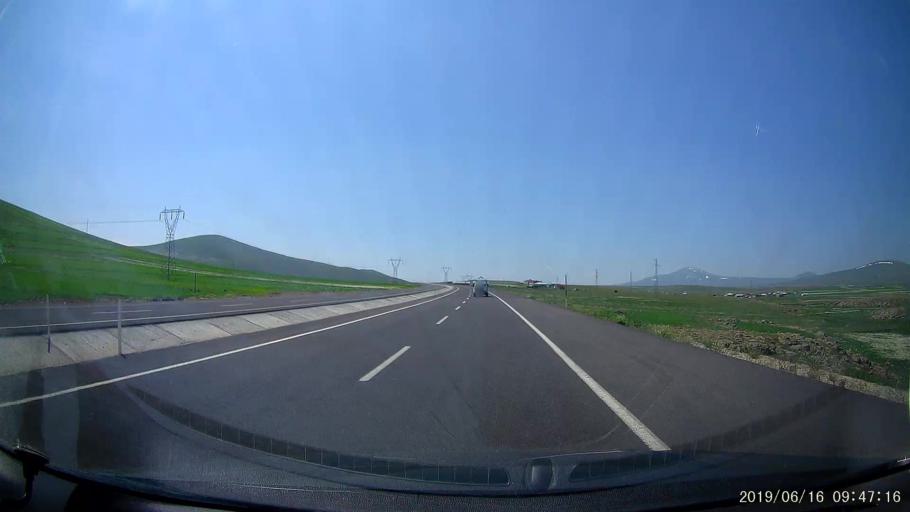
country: TR
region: Kars
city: Digor
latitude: 40.4506
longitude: 43.3422
